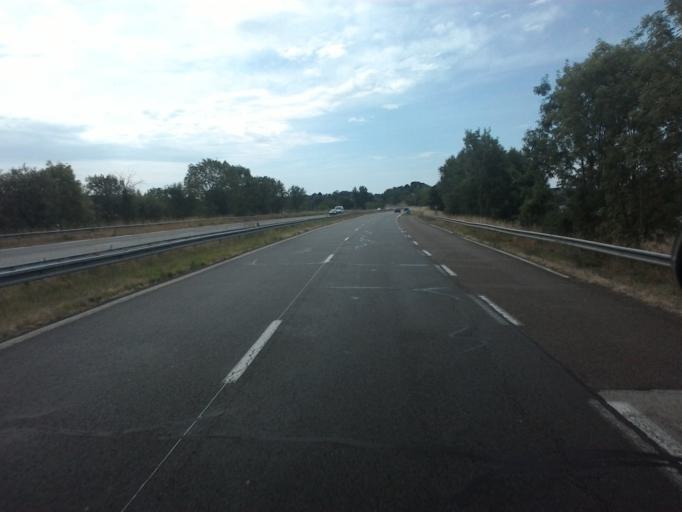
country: FR
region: Franche-Comte
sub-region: Departement du Jura
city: Montmorot
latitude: 46.7619
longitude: 5.5561
